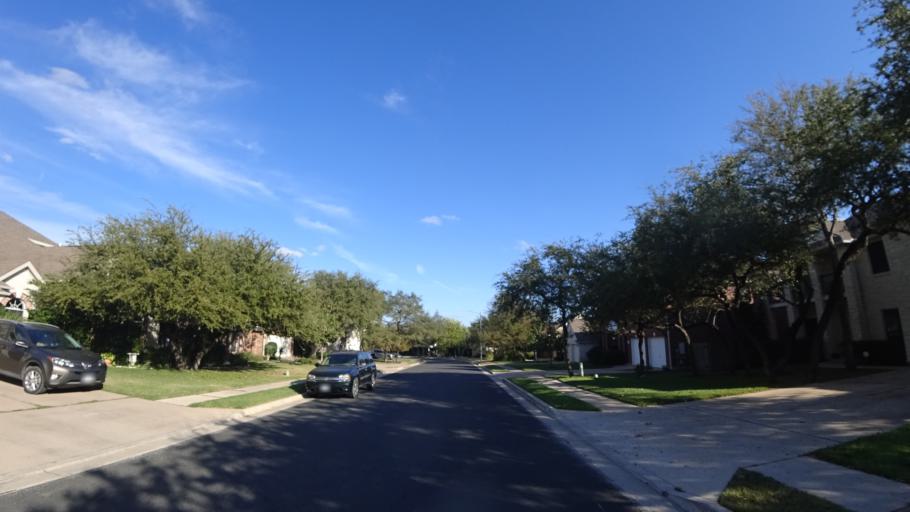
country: US
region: Texas
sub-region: Travis County
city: Barton Creek
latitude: 30.2509
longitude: -97.8436
